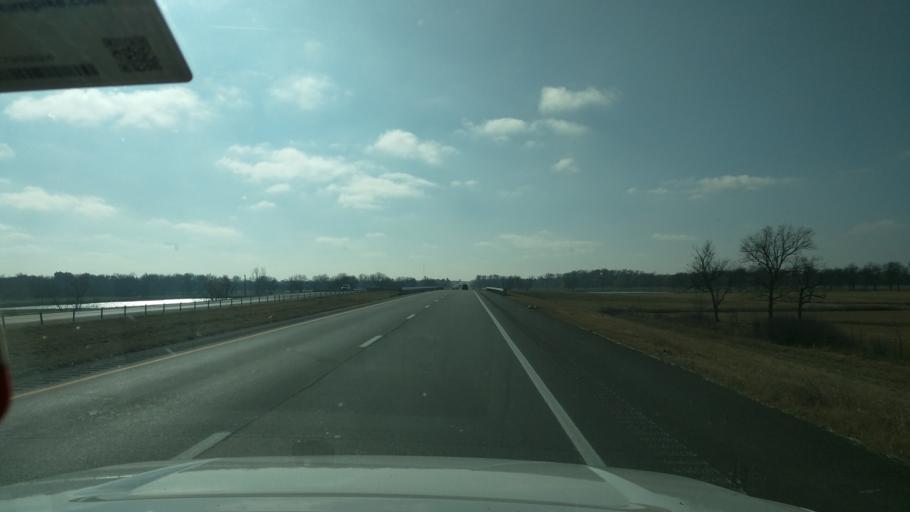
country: US
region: Oklahoma
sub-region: Washington County
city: Bartlesville
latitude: 36.6576
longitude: -95.9355
